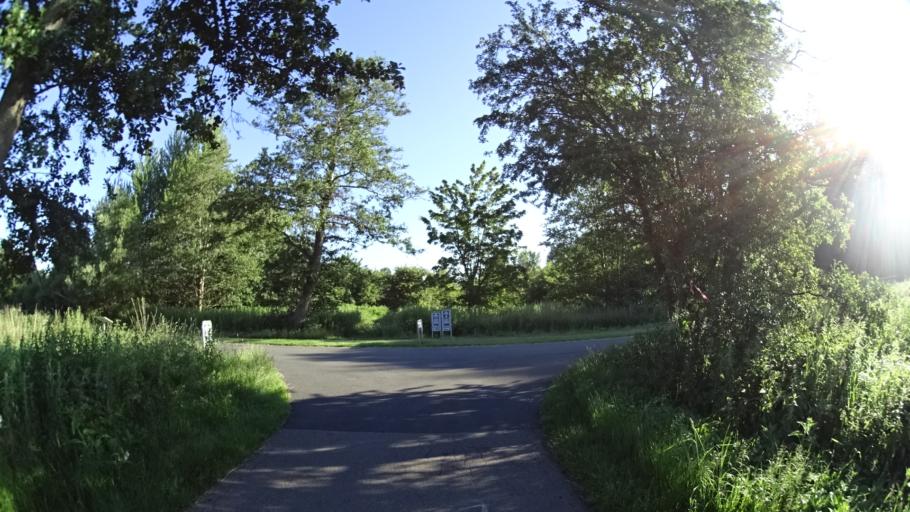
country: DK
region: Central Jutland
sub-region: Arhus Kommune
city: Stavtrup
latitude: 56.1411
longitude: 10.1446
